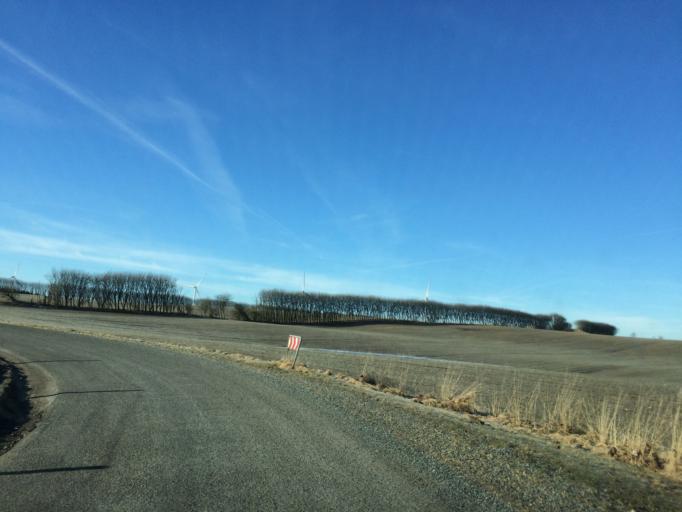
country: DK
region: North Denmark
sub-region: Mariagerfjord Kommune
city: Hobro
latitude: 56.6421
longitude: 9.6427
